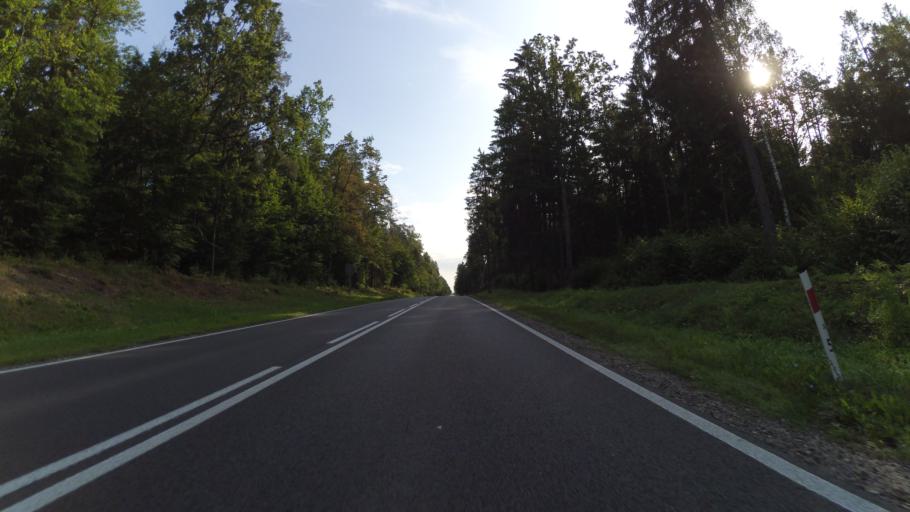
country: PL
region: Podlasie
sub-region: Powiat bialostocki
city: Czarna Bialostocka
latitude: 53.3060
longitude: 23.3123
